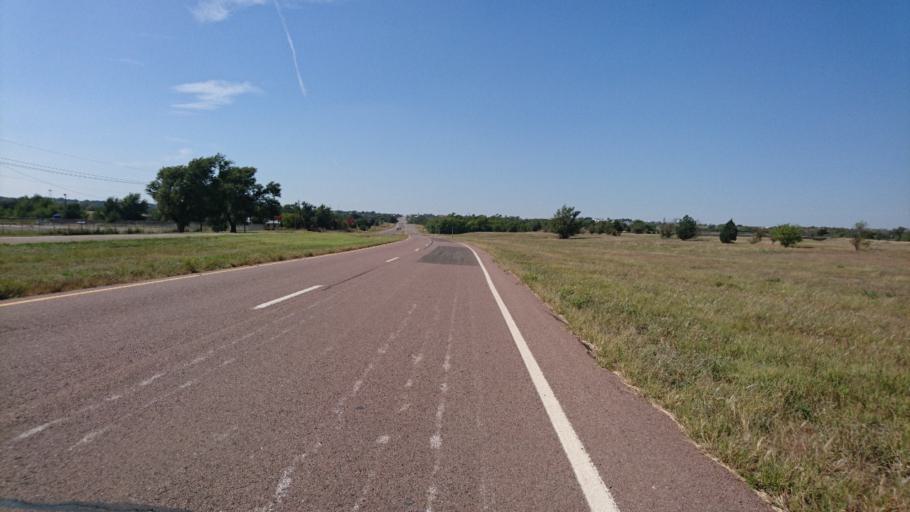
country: US
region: Texas
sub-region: Wheeler County
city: Shamrock
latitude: 35.2267
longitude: -100.2234
